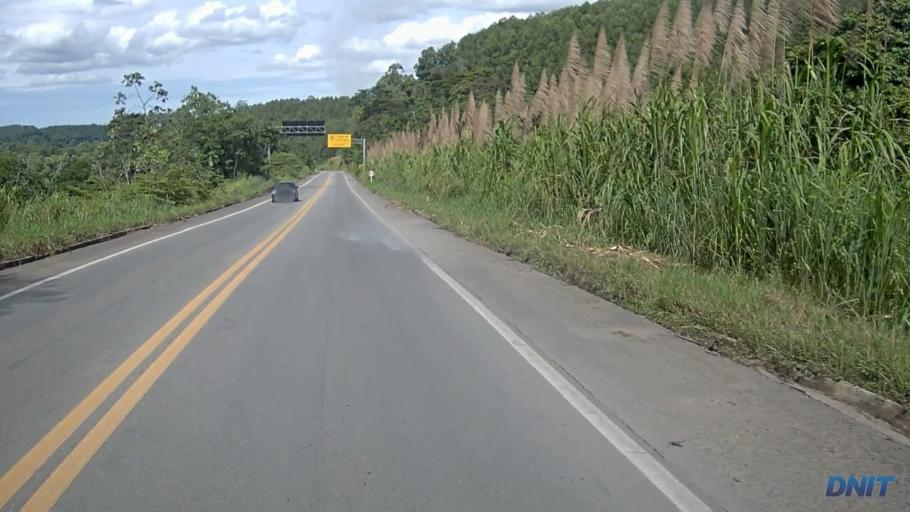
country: BR
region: Minas Gerais
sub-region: Ipaba
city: Ipaba
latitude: -19.3239
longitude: -42.4134
